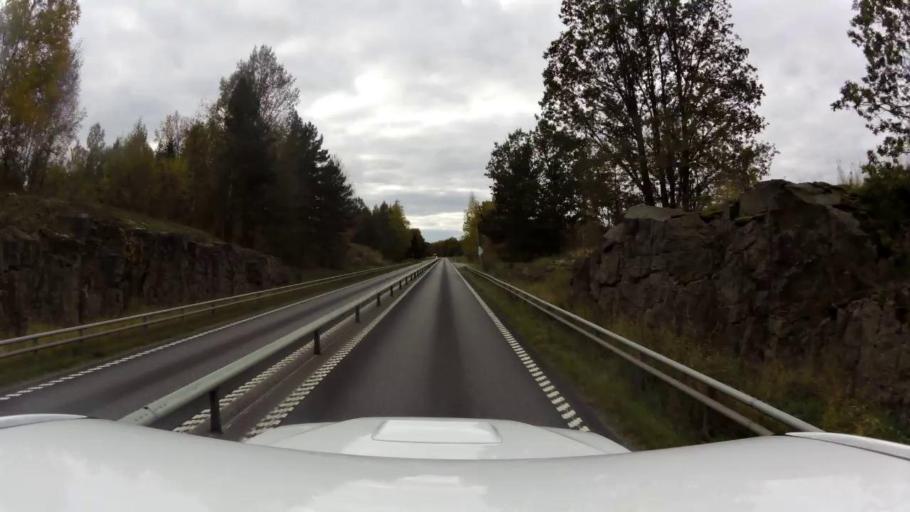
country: SE
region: OEstergoetland
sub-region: Linkopings Kommun
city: Malmslatt
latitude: 58.2975
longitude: 15.5641
